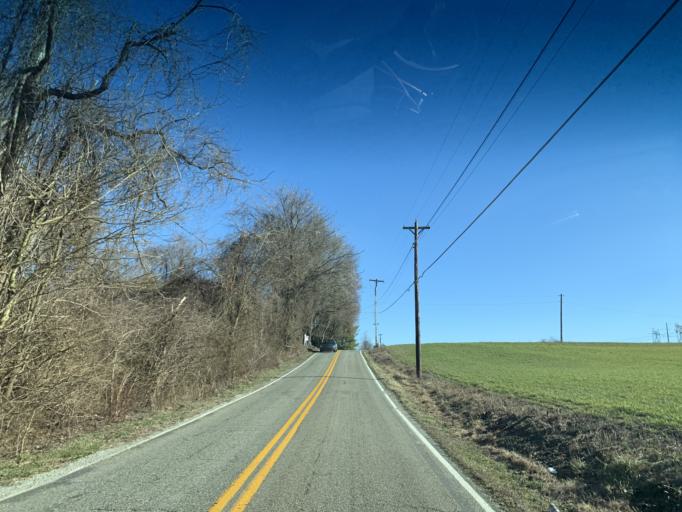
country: US
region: Maryland
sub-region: Cecil County
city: Rising Sun
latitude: 39.6849
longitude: -76.1032
